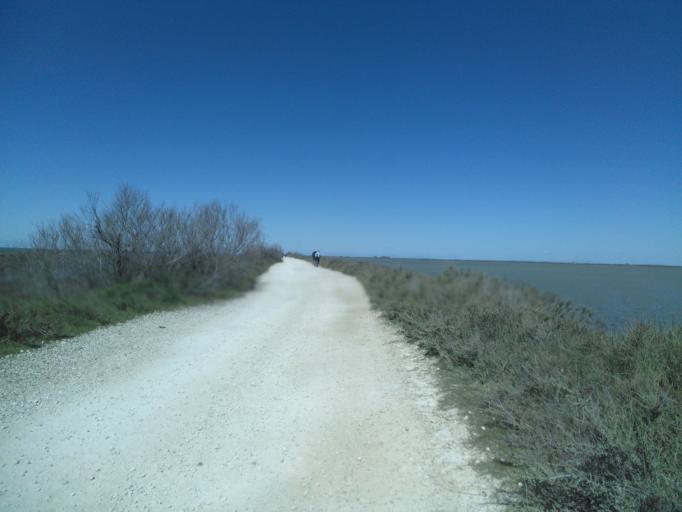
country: FR
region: Provence-Alpes-Cote d'Azur
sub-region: Departement des Bouches-du-Rhone
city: Saintes-Maries-de-la-Mer
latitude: 43.4428
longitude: 4.6104
